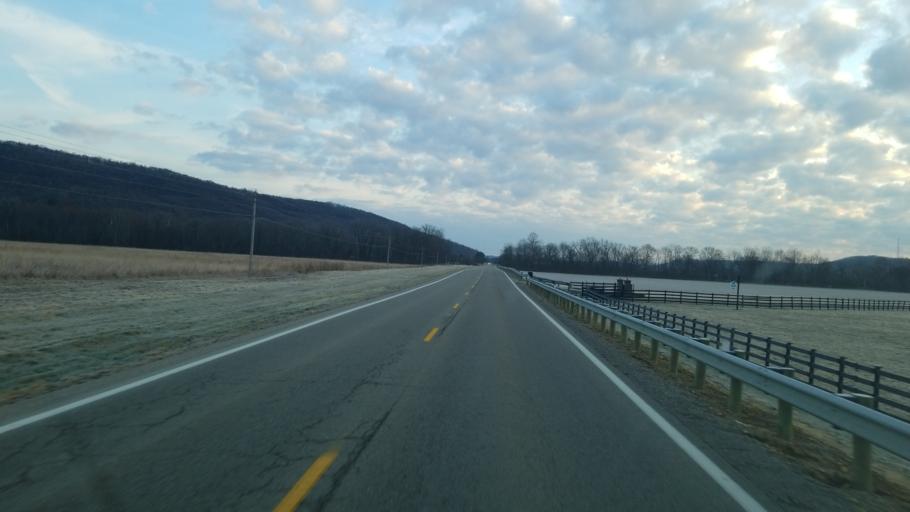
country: US
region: Ohio
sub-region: Ross County
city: Frankfort
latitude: 39.2376
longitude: -83.2361
